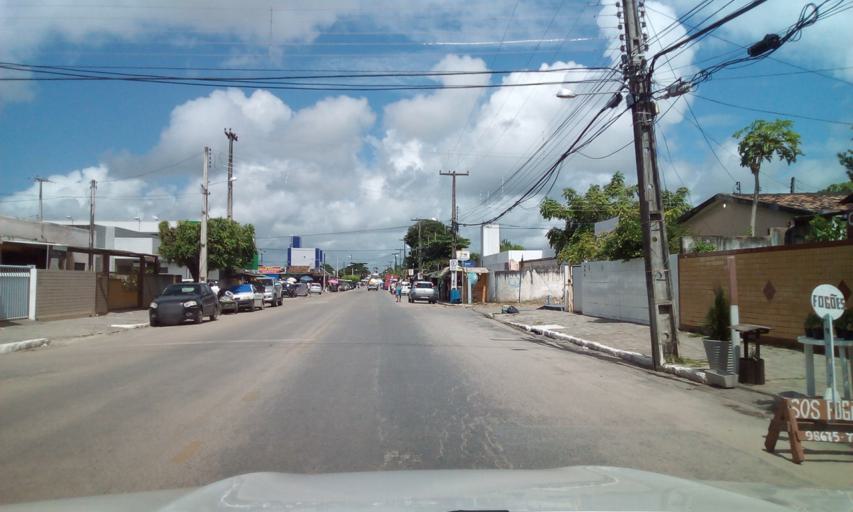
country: BR
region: Paraiba
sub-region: Joao Pessoa
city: Joao Pessoa
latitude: -7.1762
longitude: -34.8689
